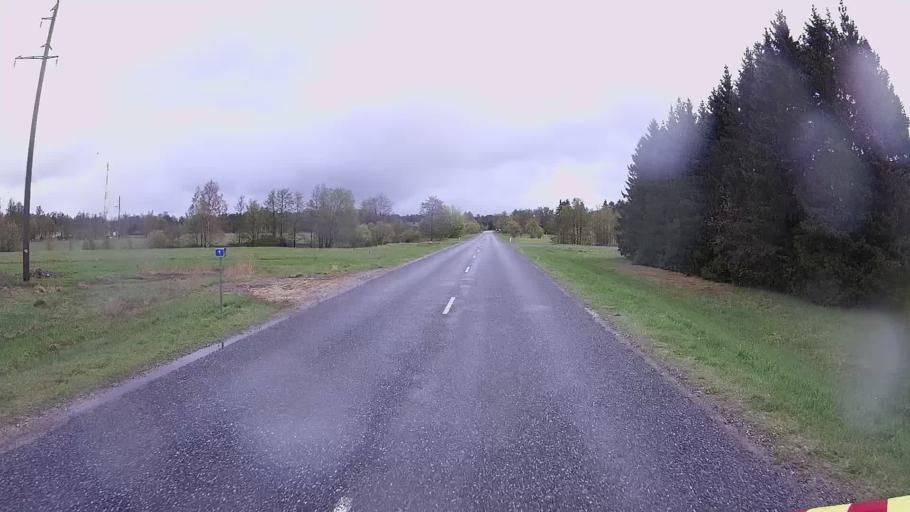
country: EE
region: Hiiumaa
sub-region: Kaerdla linn
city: Kardla
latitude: 58.7015
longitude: 22.5824
